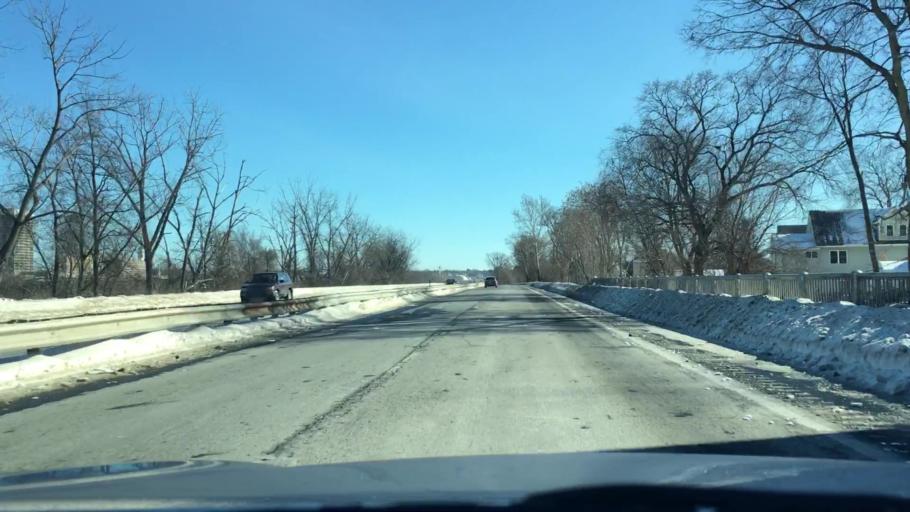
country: US
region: Massachusetts
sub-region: Hampden County
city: West Springfield
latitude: 42.1032
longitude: -72.6085
